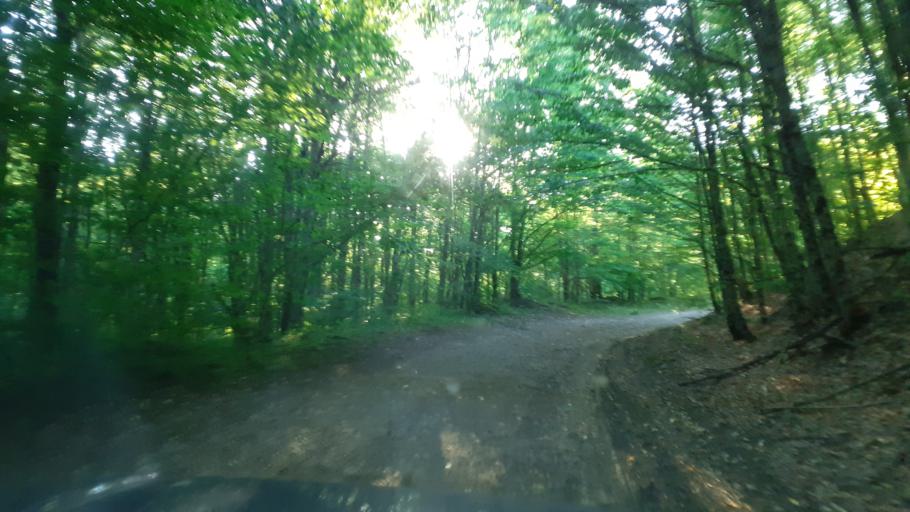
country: RU
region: Krasnodarskiy
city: Pshada
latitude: 44.6566
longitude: 38.4504
